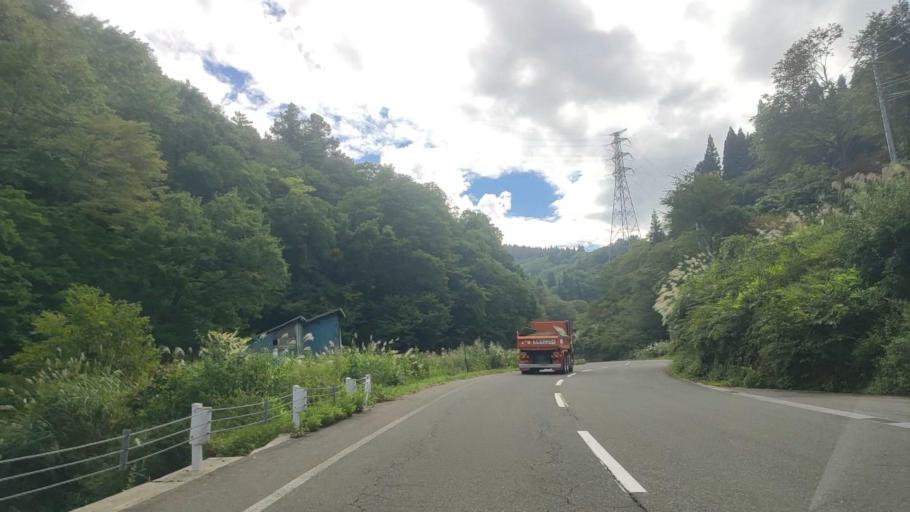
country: JP
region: Nagano
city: Iiyama
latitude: 36.8929
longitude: 138.3223
